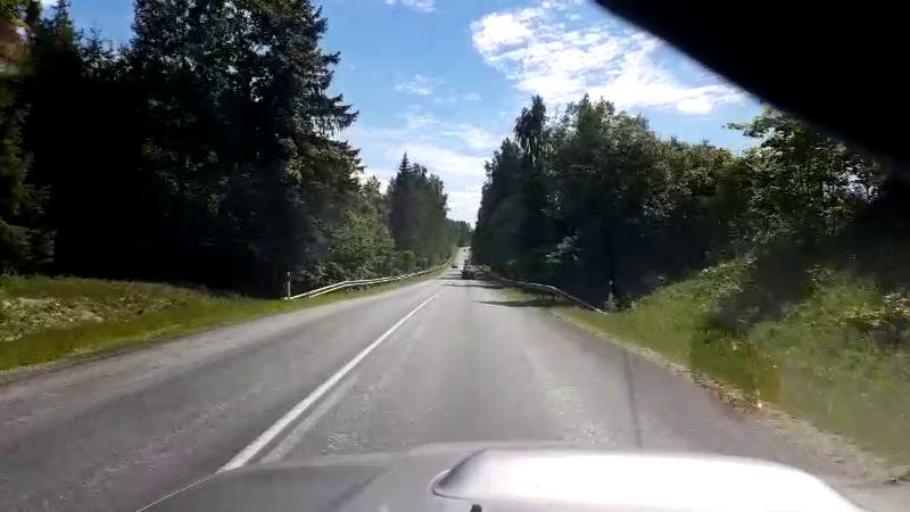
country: EE
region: Laeaene-Virumaa
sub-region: Rakke vald
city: Rakke
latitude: 58.8457
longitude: 26.2909
